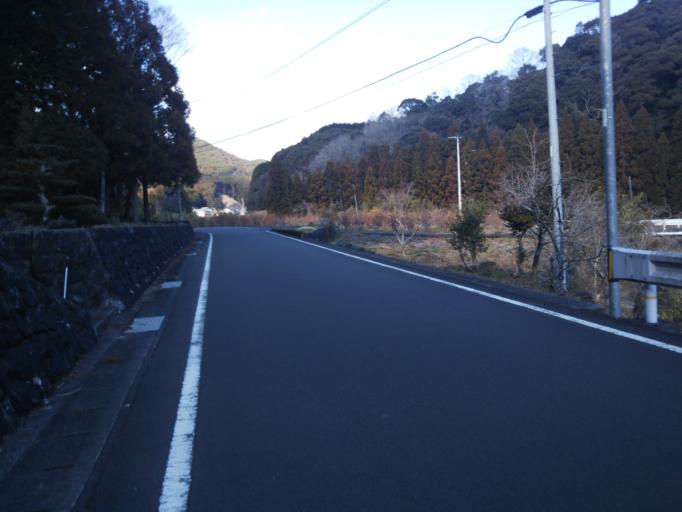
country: JP
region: Kochi
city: Nakamura
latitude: 33.0438
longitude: 132.9707
